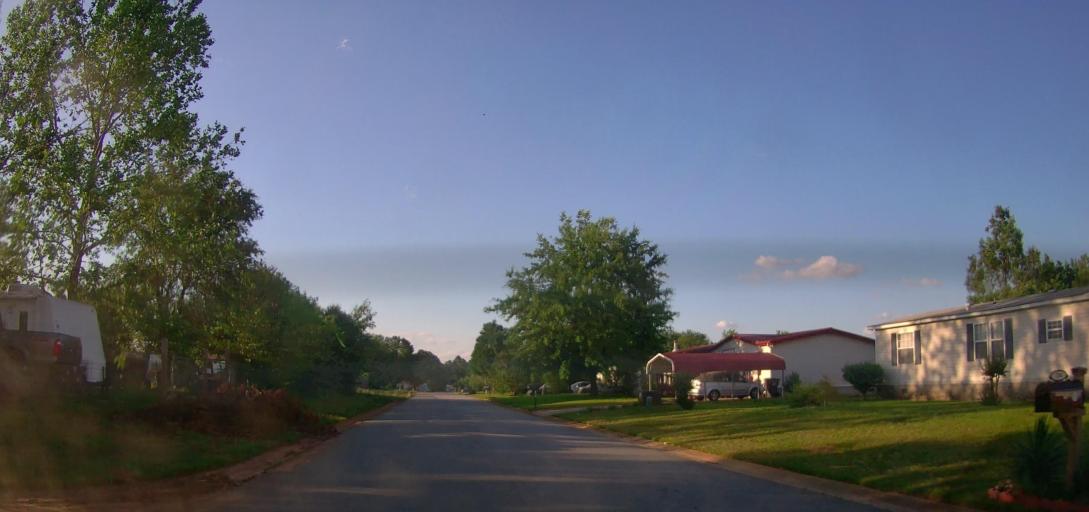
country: US
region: Georgia
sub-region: Houston County
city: Centerville
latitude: 32.6396
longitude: -83.7241
